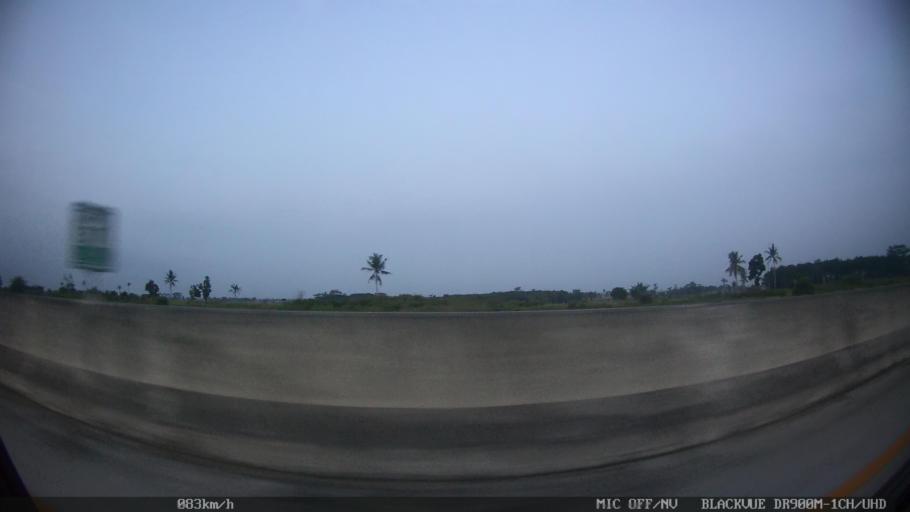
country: ID
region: Lampung
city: Sidorejo
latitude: -5.6179
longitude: 105.5617
